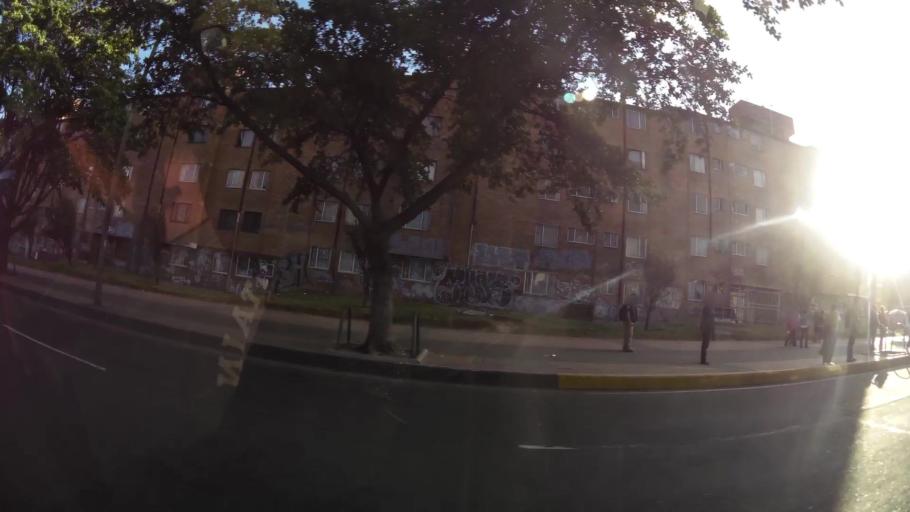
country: CO
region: Cundinamarca
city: Soacha
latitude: 4.5705
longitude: -74.1488
